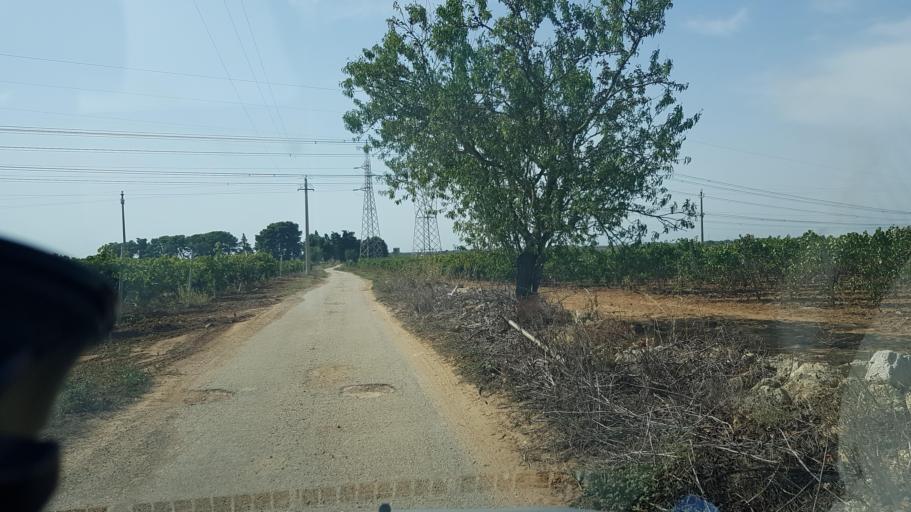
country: IT
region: Apulia
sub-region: Provincia di Brindisi
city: Brindisi
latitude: 40.6017
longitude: 17.8865
